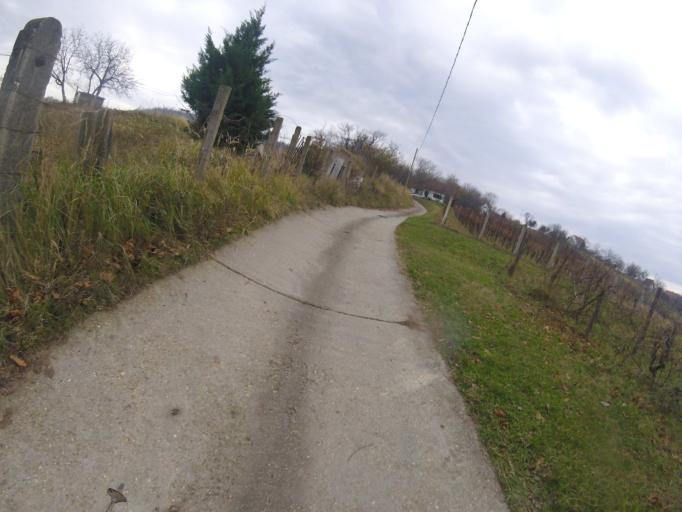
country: HU
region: Tolna
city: Szekszard
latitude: 46.3264
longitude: 18.6876
